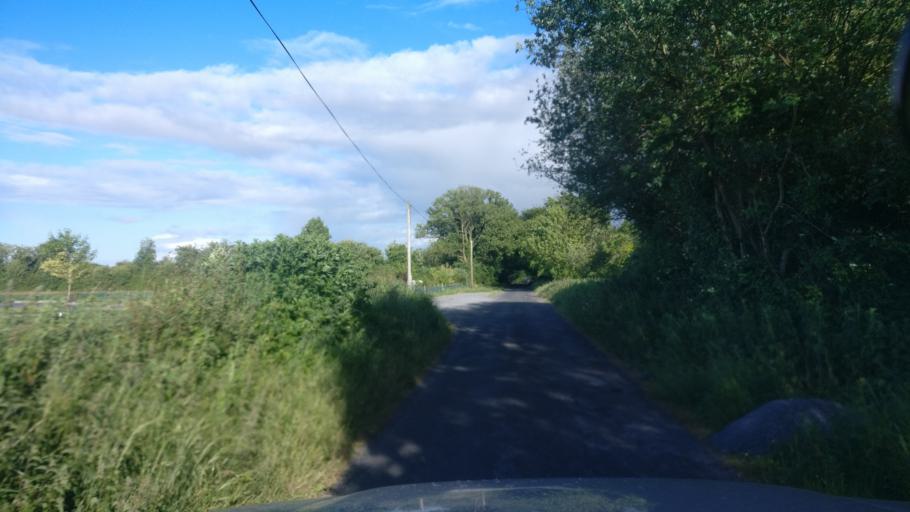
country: IE
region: Connaught
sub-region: County Galway
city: Ballinasloe
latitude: 53.2392
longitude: -8.1842
